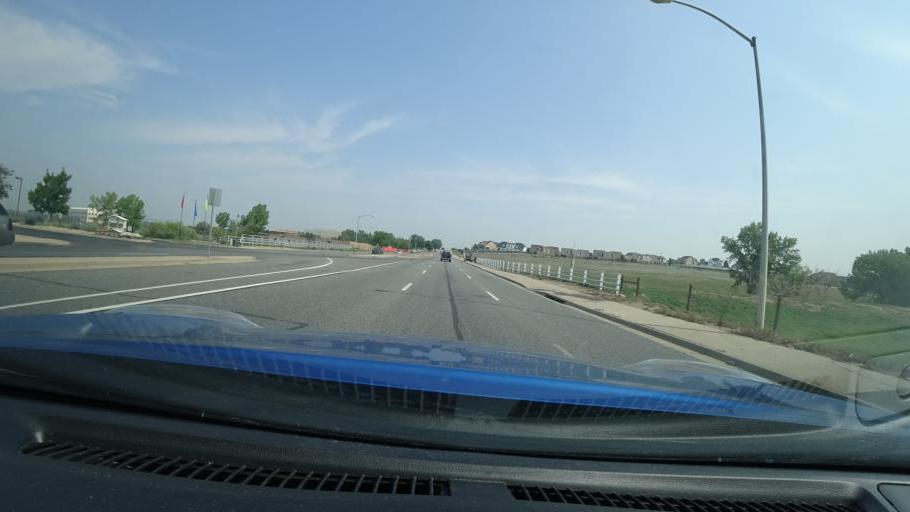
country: US
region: Colorado
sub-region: Adams County
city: Aurora
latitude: 39.7108
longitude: -104.7911
